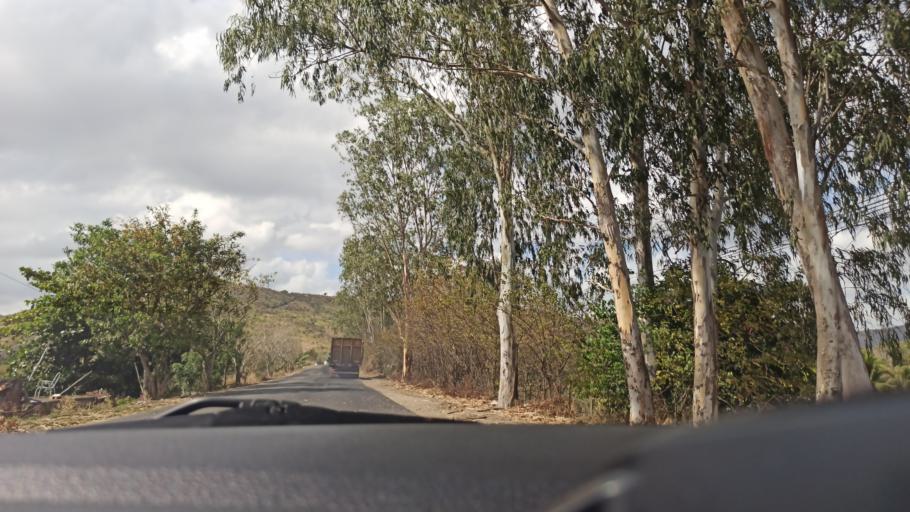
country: BR
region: Pernambuco
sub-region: Timbauba
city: Timbauba
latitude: -7.5157
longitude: -35.3040
